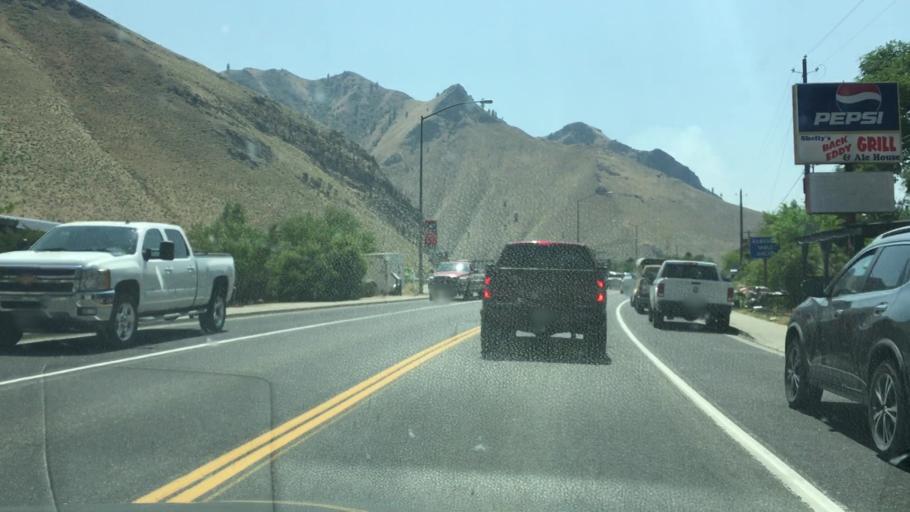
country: US
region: Idaho
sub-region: Idaho County
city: Grangeville
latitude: 45.4266
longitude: -116.3120
